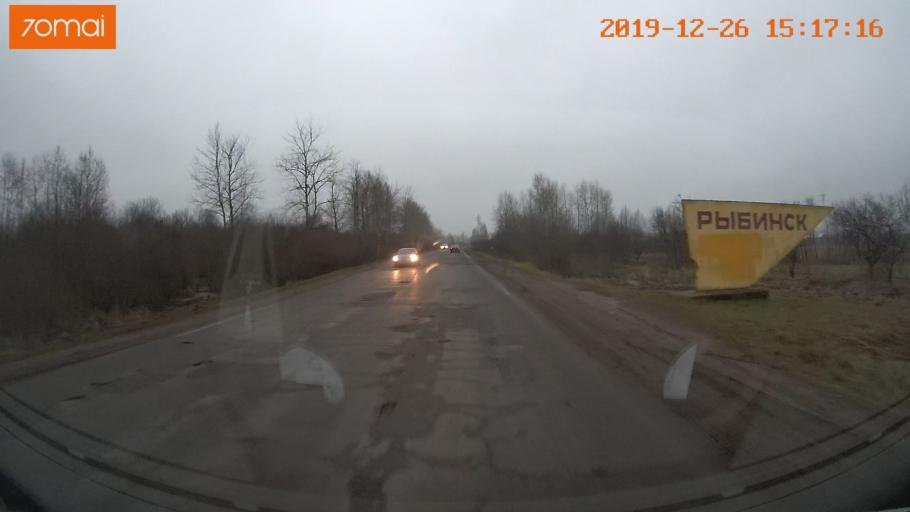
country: RU
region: Jaroslavl
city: Rybinsk
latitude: 58.0788
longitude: 38.8525
